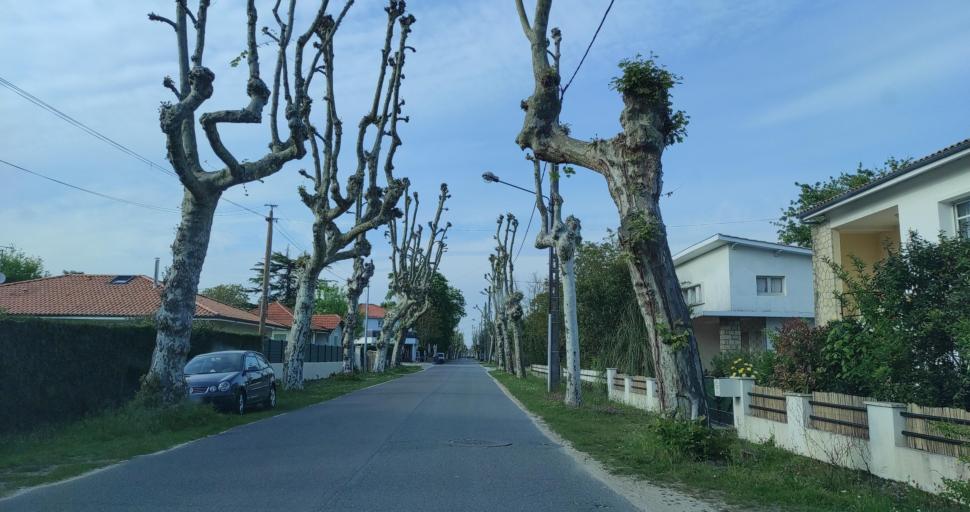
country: FR
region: Aquitaine
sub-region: Departement de la Gironde
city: Ares
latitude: 44.7573
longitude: -1.1332
